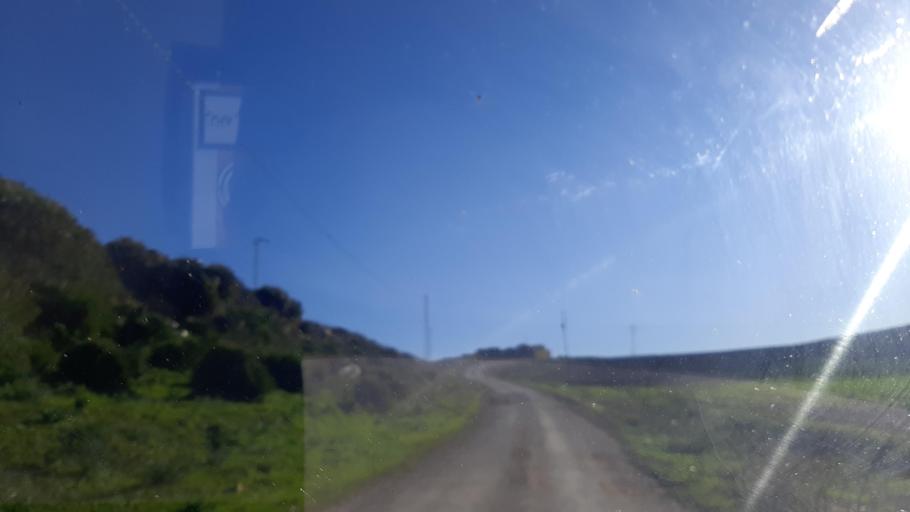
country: TN
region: Nabul
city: El Mida
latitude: 36.8091
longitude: 10.8458
